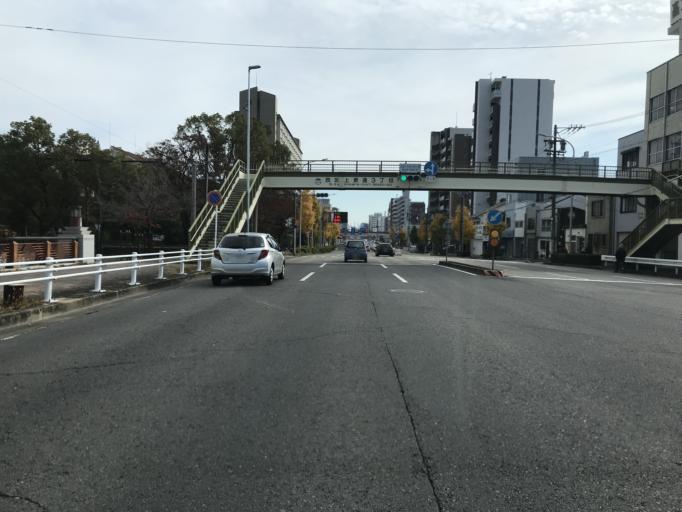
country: JP
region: Aichi
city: Nagoya-shi
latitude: 35.1887
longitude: 136.8728
